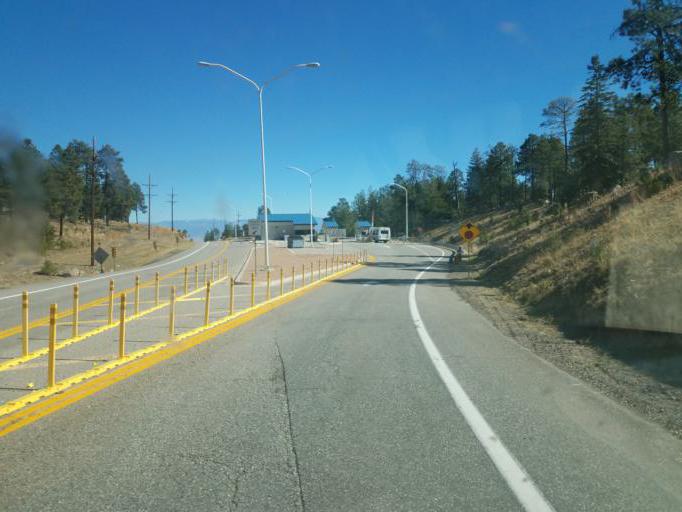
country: US
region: New Mexico
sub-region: Los Alamos County
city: Los Alamos
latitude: 35.8726
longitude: -106.3463
